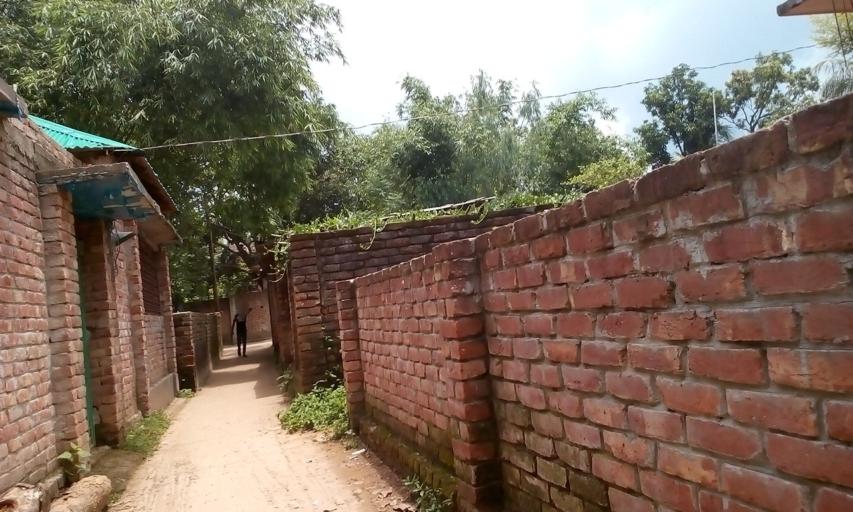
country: IN
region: West Bengal
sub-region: Dakshin Dinajpur
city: Balurghat
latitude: 25.3827
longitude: 88.9961
